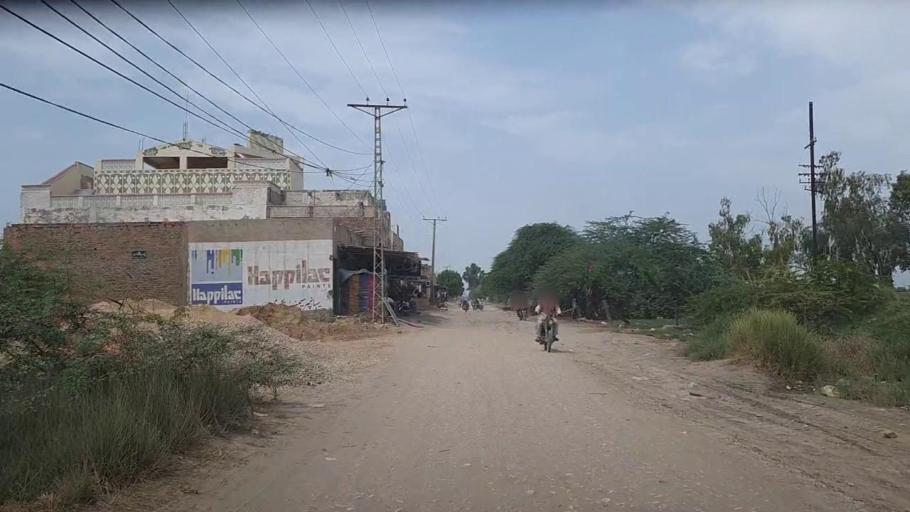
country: PK
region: Sindh
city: Bhiria
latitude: 26.8939
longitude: 68.2857
